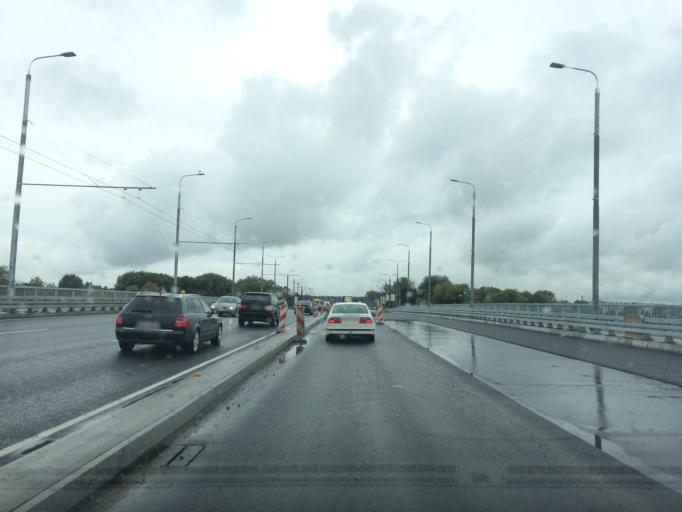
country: LV
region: Riga
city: Riga
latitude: 56.9312
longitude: 24.1176
